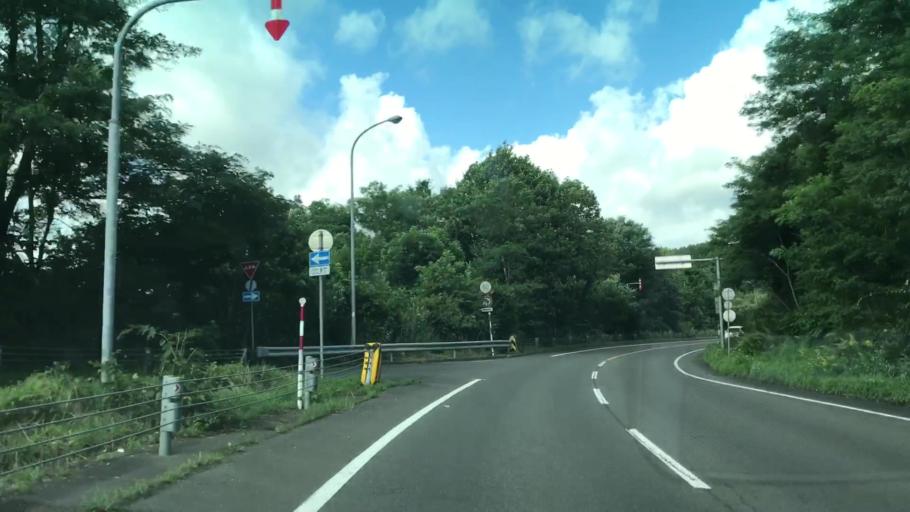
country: JP
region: Hokkaido
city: Muroran
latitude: 42.3755
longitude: 140.9626
